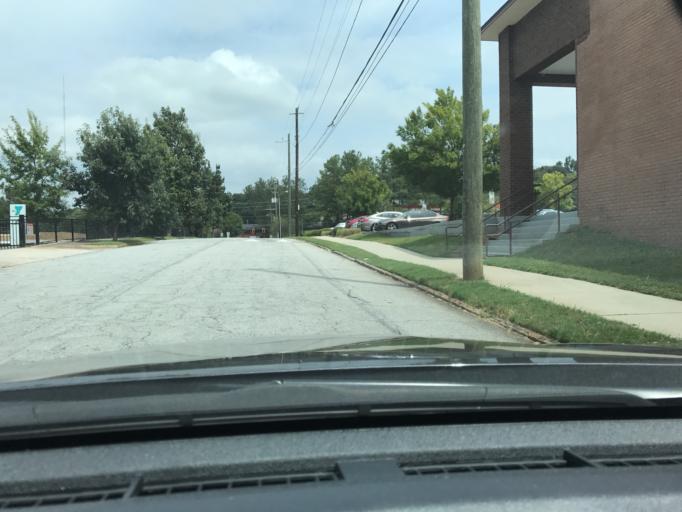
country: US
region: Georgia
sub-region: DeKalb County
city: Druid Hills
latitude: 33.7458
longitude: -84.3287
